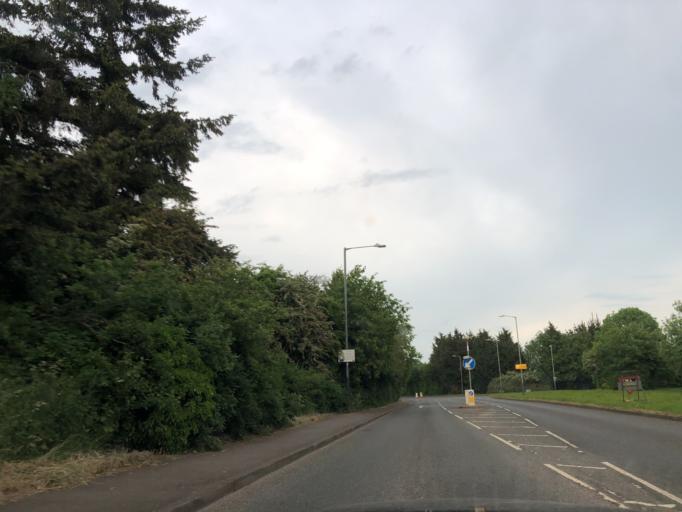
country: GB
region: England
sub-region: Warwickshire
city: Warwick
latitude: 52.2738
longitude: -1.6085
